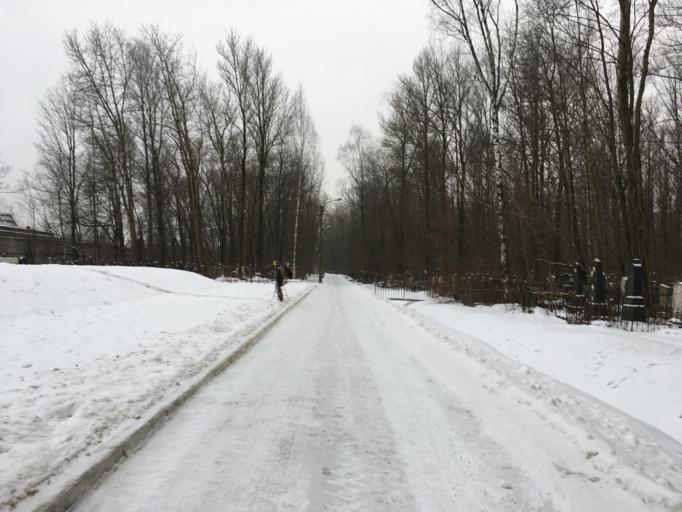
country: RU
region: St.-Petersburg
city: Obukhovo
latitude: 59.8571
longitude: 30.4539
